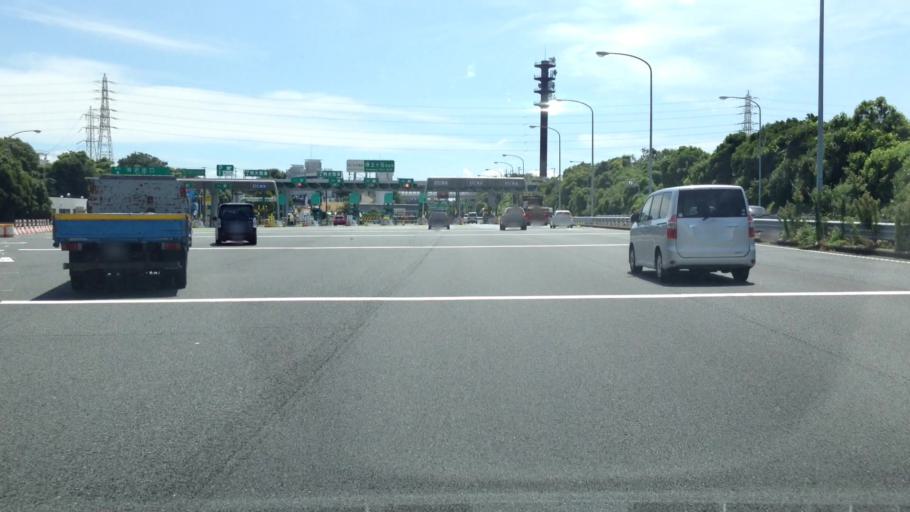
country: JP
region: Kanagawa
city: Yokohama
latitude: 35.4853
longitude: 139.5932
